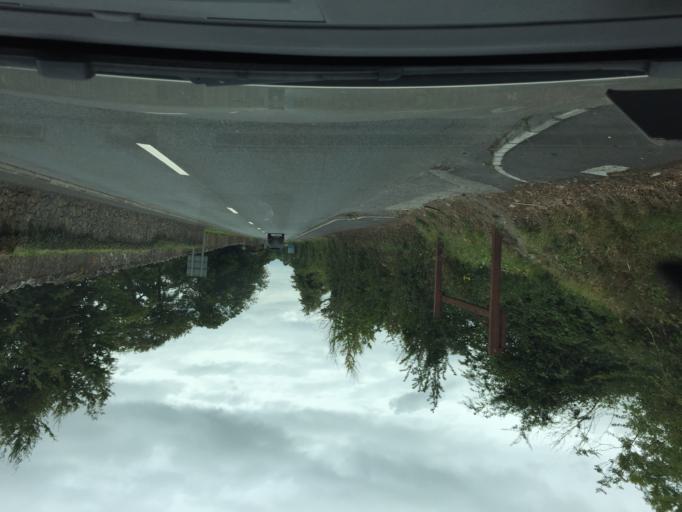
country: IE
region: Leinster
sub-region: Kildare
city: Maynooth
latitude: 53.3845
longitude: -6.5739
